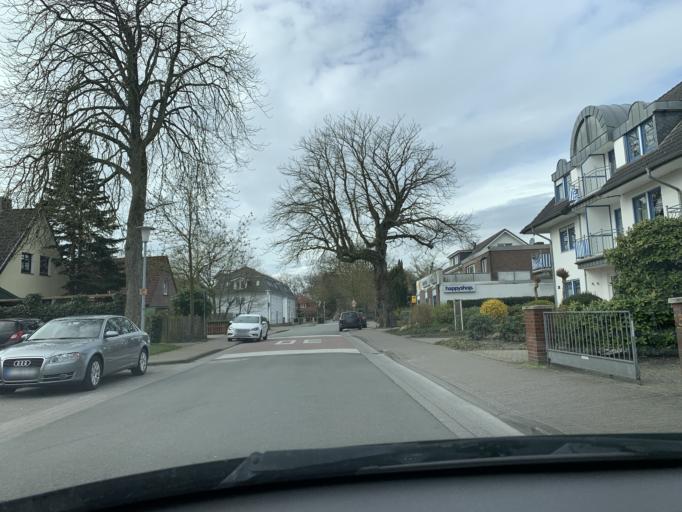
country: DE
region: Lower Saxony
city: Oldenburg
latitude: 53.1260
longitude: 8.2012
